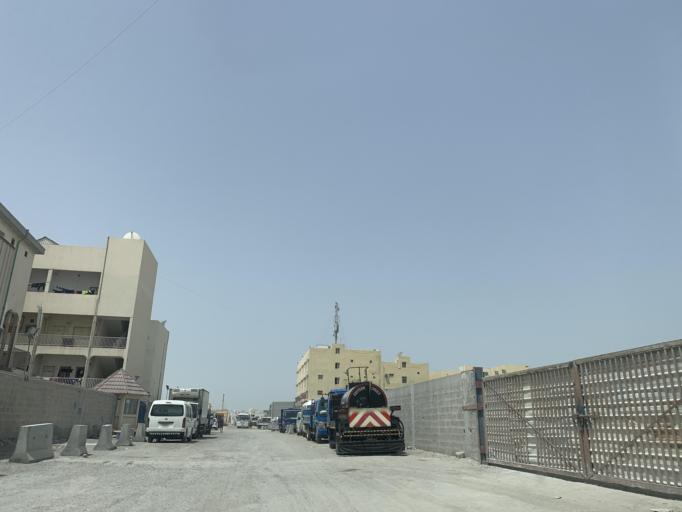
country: BH
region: Northern
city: Sitrah
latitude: 26.1456
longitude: 50.5962
